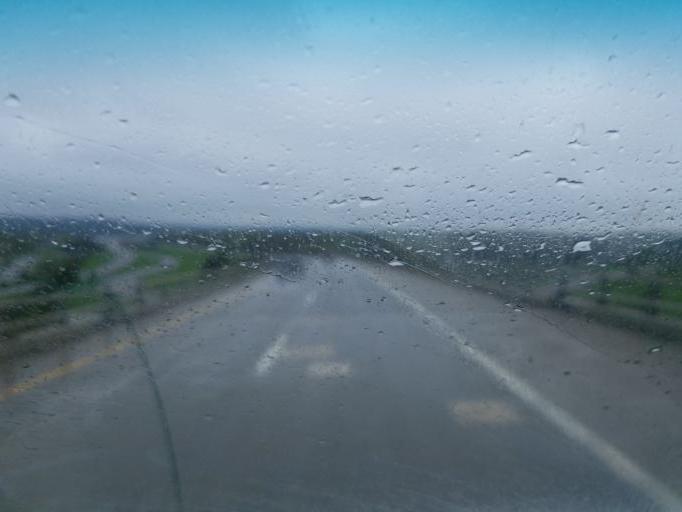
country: US
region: New York
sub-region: Chautauqua County
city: Lakewood
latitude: 42.1537
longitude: -79.3730
